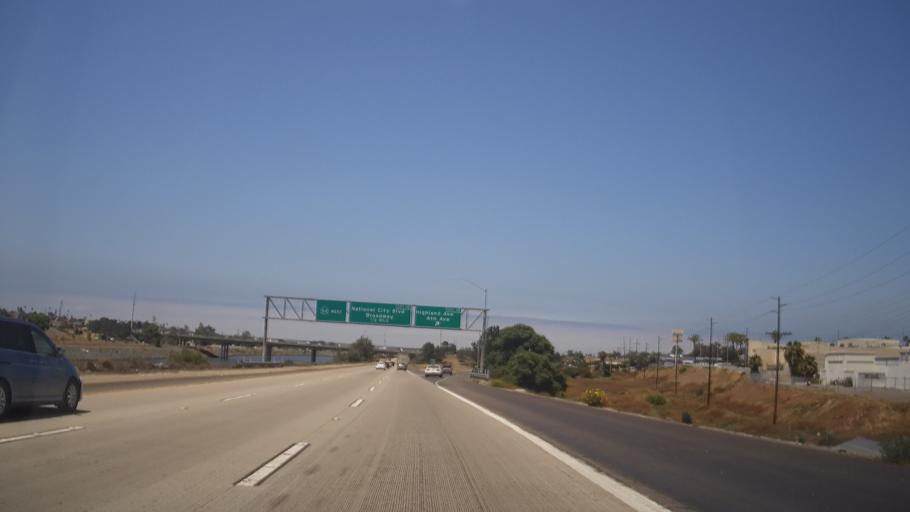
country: US
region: California
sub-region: San Diego County
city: Chula Vista
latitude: 32.6586
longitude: -117.0855
